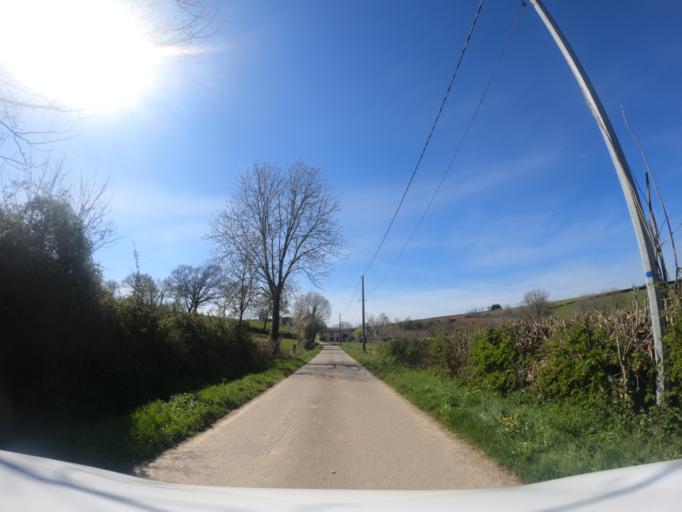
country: FR
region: Pays de la Loire
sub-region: Departement de la Vendee
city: Saint-Pierre-du-Chemin
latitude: 46.6708
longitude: -0.6979
